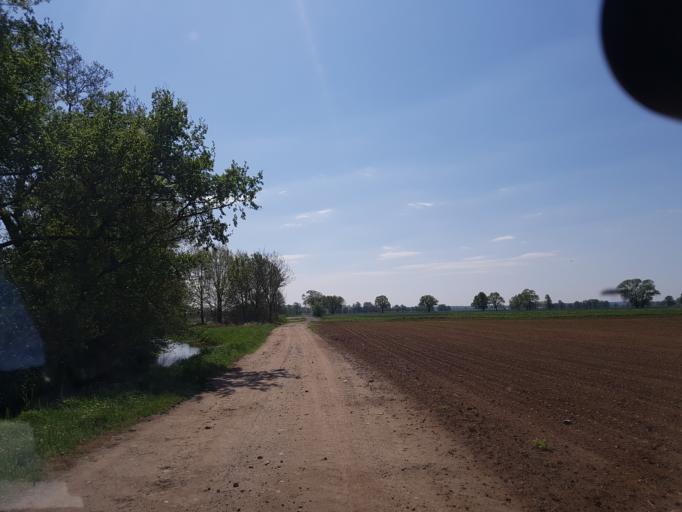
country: DE
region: Brandenburg
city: Schonewalde
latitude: 51.6778
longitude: 13.5834
